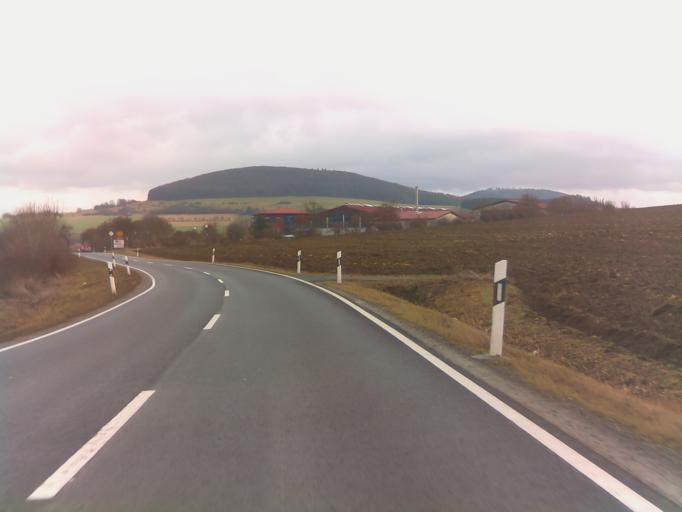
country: DE
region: Thuringia
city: Kaltensundheim
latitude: 50.6070
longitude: 10.1453
